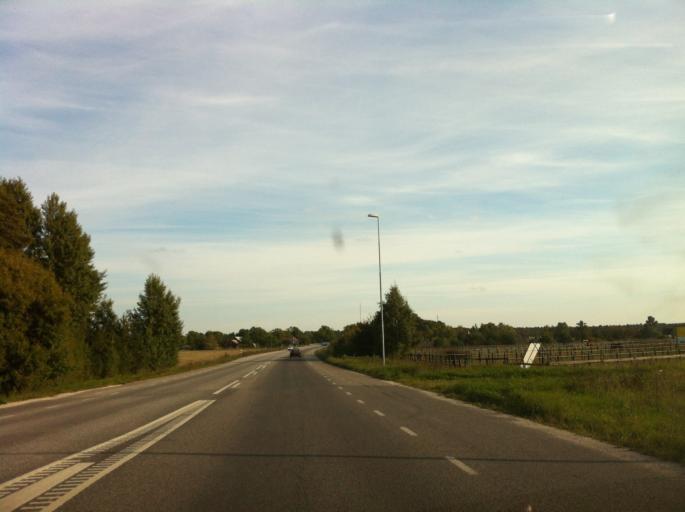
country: SE
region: Gotland
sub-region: Gotland
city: Visby
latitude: 57.6228
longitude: 18.3266
